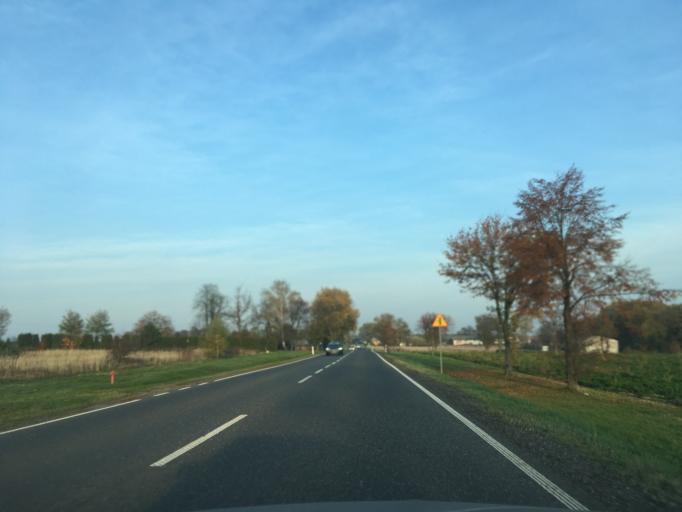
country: PL
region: Lodz Voivodeship
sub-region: Powiat skierniewicki
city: Kowiesy
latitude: 51.9215
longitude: 20.4104
